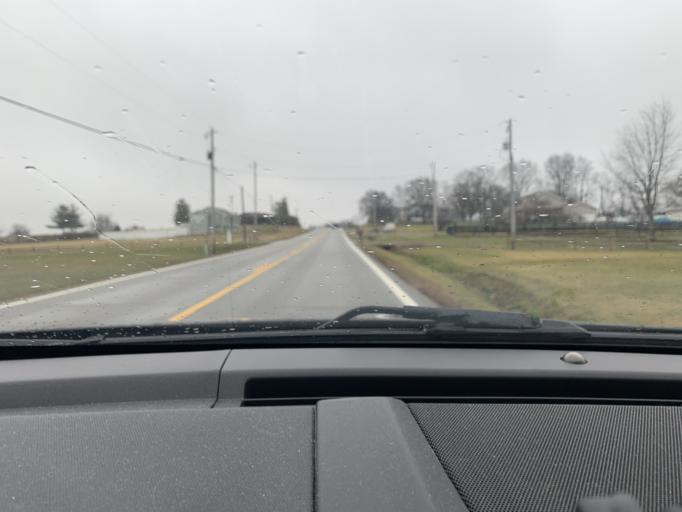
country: US
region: Ohio
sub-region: Ross County
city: Kingston
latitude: 39.4320
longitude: -82.9053
